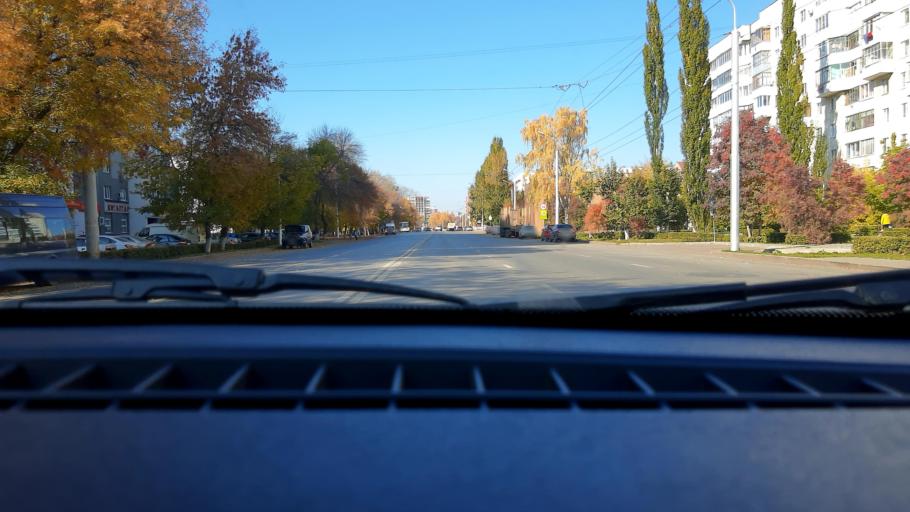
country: RU
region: Bashkortostan
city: Mikhaylovka
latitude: 54.7822
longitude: 55.8878
